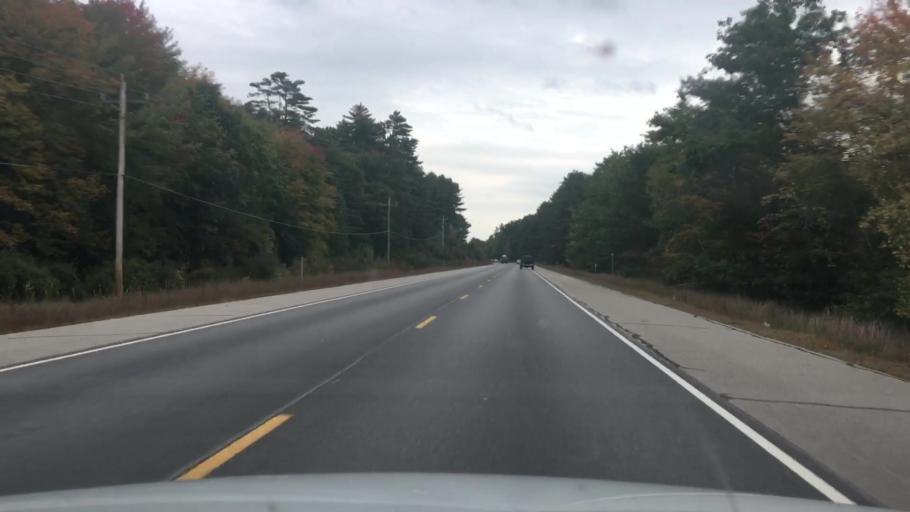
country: US
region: New Hampshire
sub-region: Strafford County
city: New Durham
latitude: 43.4445
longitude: -71.1996
